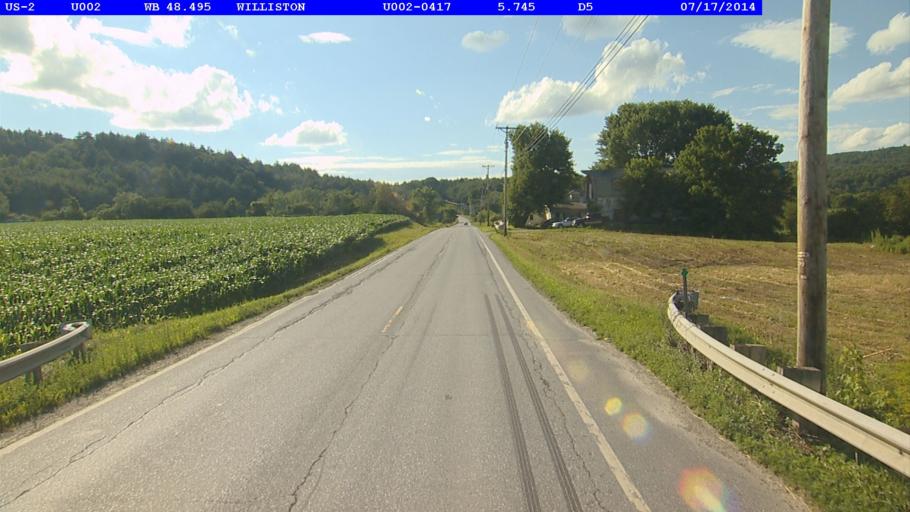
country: US
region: Vermont
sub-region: Chittenden County
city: Williston
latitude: 44.4305
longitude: -73.0308
